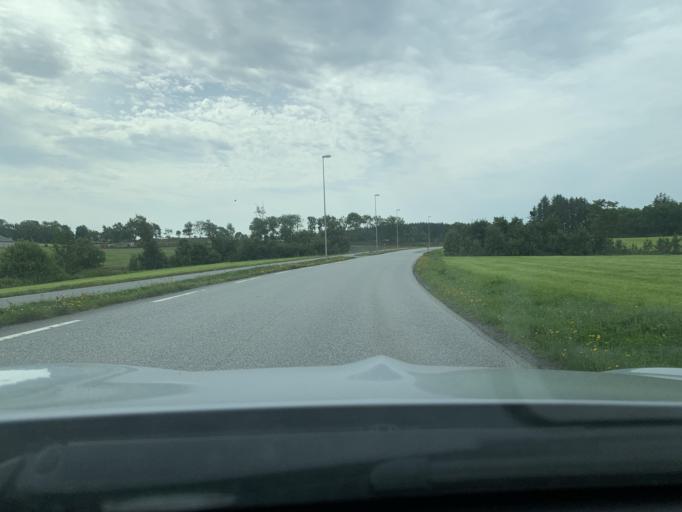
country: NO
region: Rogaland
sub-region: Time
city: Bryne
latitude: 58.7578
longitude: 5.7093
